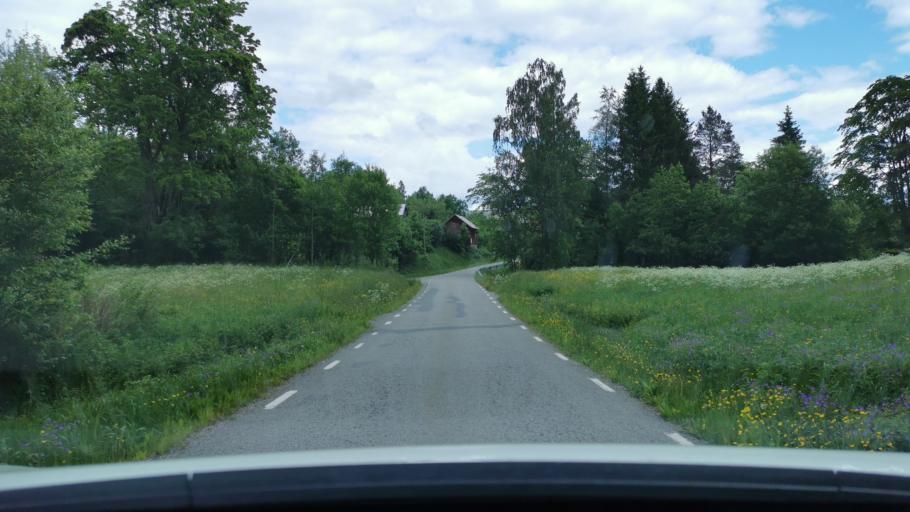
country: SE
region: Vaestra Goetaland
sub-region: Bengtsfors Kommun
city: Dals Langed
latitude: 58.8390
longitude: 12.3305
